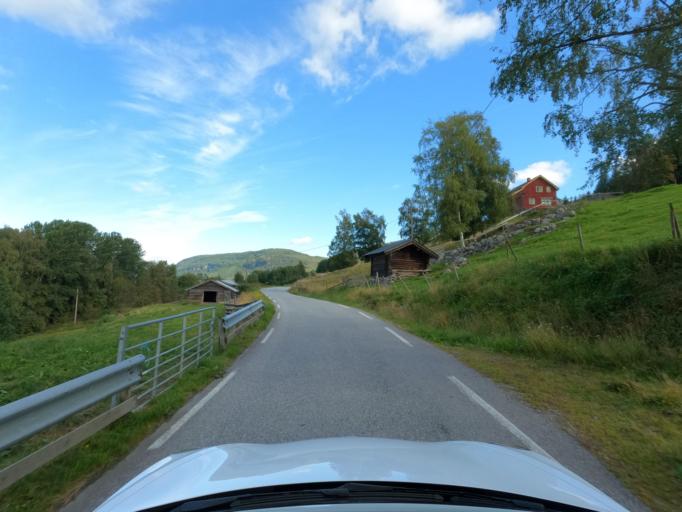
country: NO
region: Buskerud
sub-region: Nore og Uvdal
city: Rodberg
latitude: 60.0355
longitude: 8.8331
